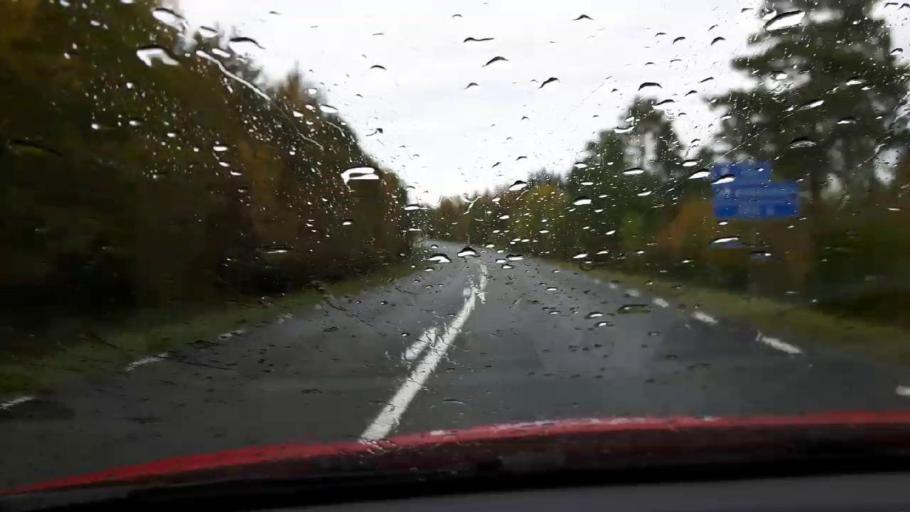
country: SE
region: Jaemtland
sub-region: Krokoms Kommun
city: Krokom
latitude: 63.1225
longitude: 14.2940
